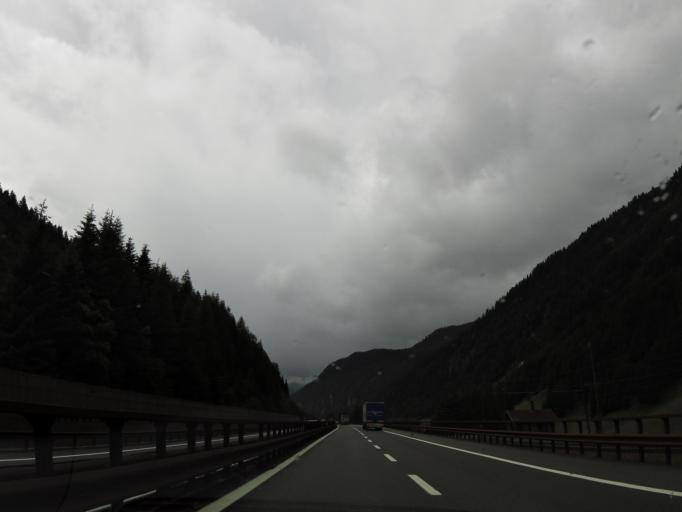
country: IT
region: Trentino-Alto Adige
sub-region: Bolzano
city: Ried
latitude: 46.9808
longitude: 11.4900
